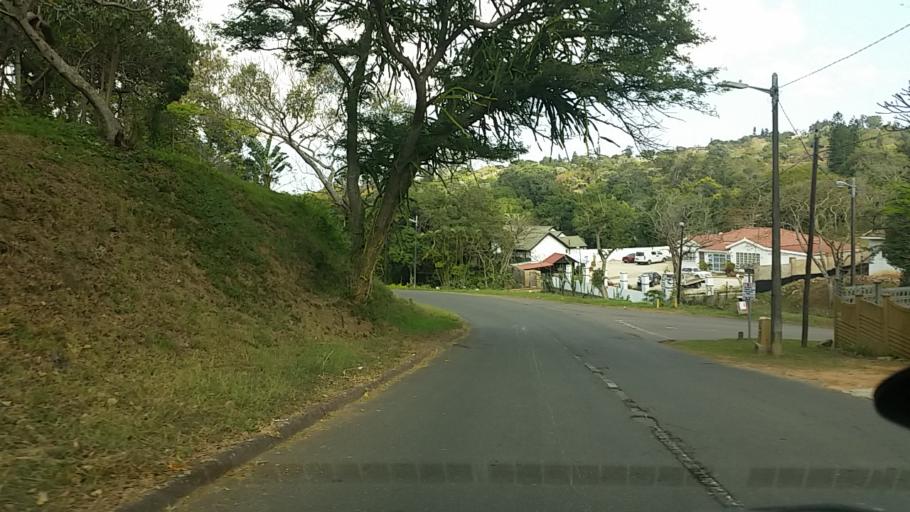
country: ZA
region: KwaZulu-Natal
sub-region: eThekwini Metropolitan Municipality
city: Berea
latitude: -29.8368
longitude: 30.9529
